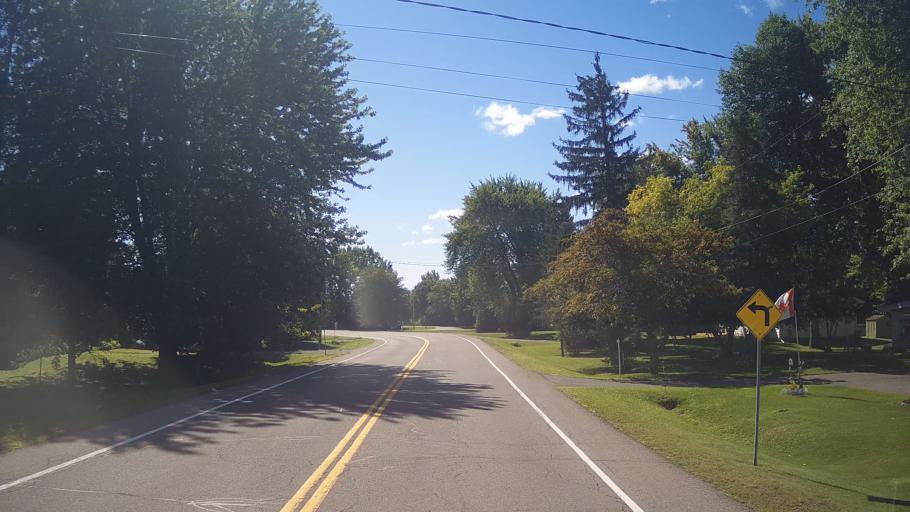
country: US
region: New York
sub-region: St. Lawrence County
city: Norfolk
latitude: 44.9723
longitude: -75.2531
